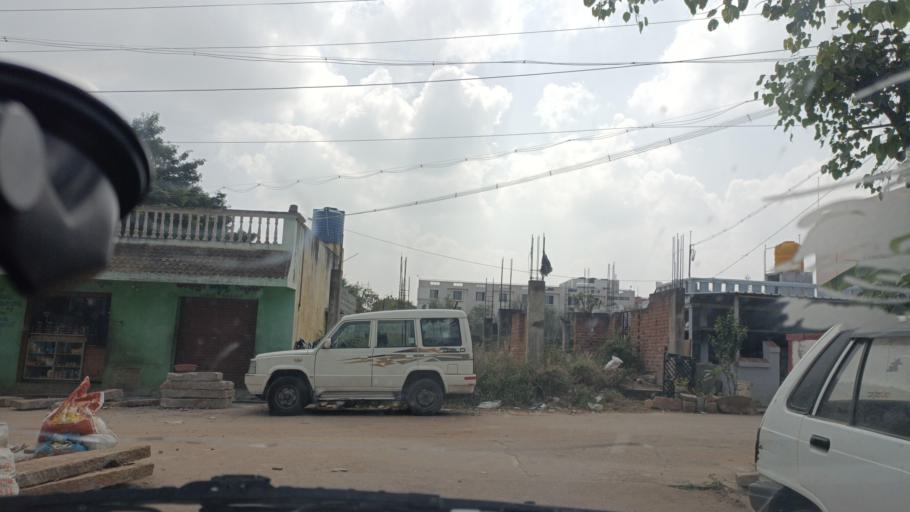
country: IN
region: Karnataka
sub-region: Bangalore Urban
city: Yelahanka
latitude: 13.1635
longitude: 77.6361
